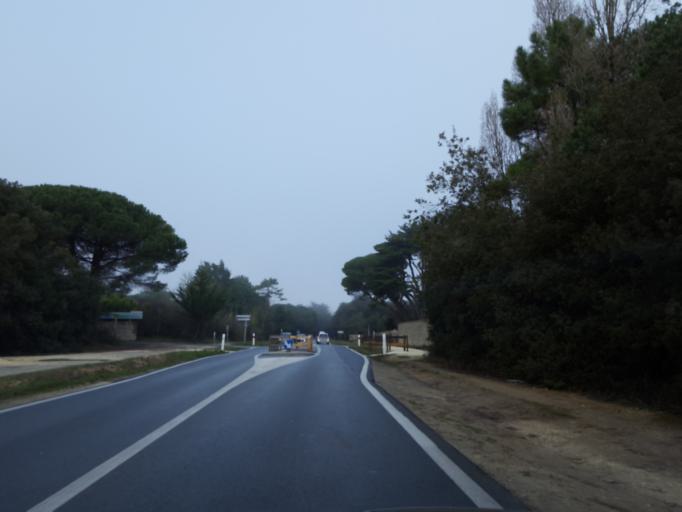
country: FR
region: Poitou-Charentes
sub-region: Departement de la Charente-Maritime
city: La Flotte
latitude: 46.1873
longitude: -1.3428
